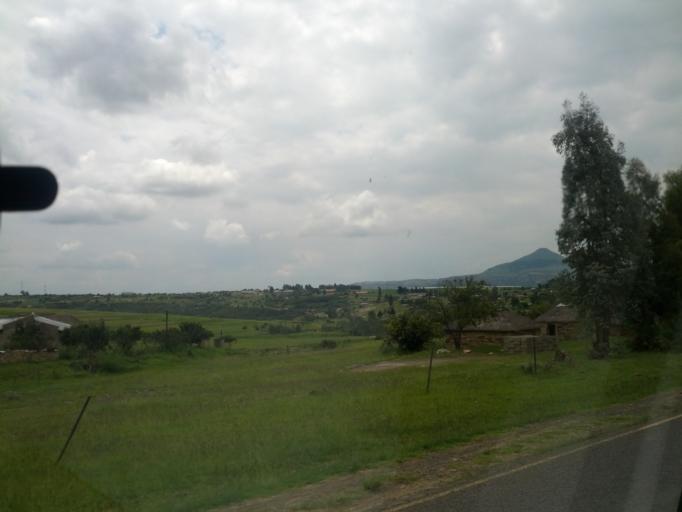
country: LS
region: Leribe
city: Leribe
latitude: -28.9458
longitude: 28.1699
